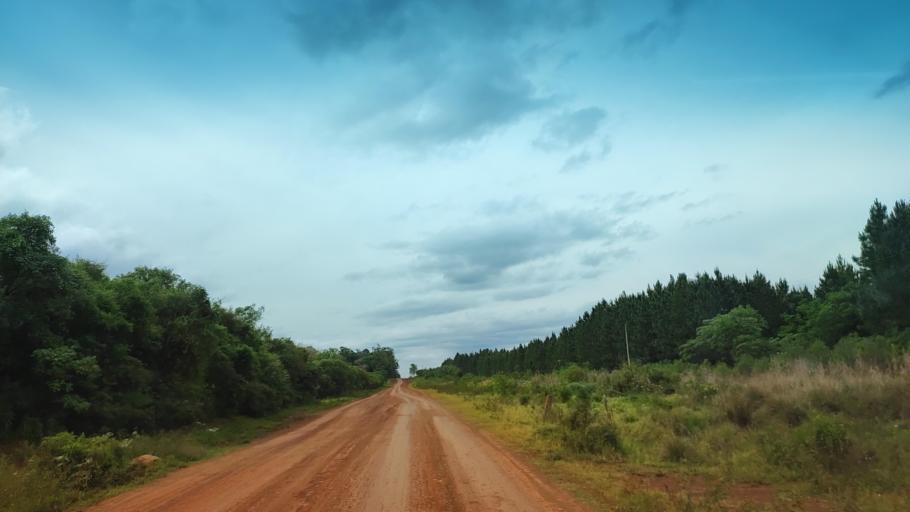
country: AR
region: Misiones
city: Garupa
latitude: -27.4996
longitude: -55.9708
